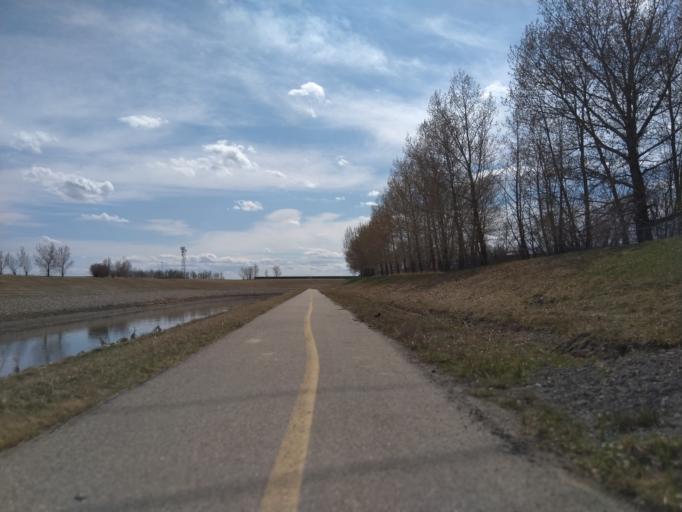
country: CA
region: Alberta
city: Chestermere
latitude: 50.9651
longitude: -113.9515
